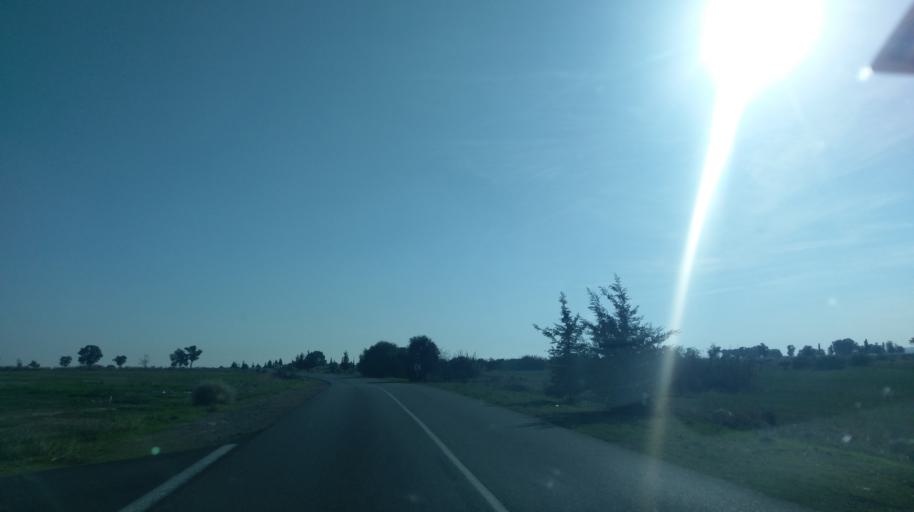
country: CY
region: Larnaka
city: Pergamos
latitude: 35.0829
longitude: 33.7210
